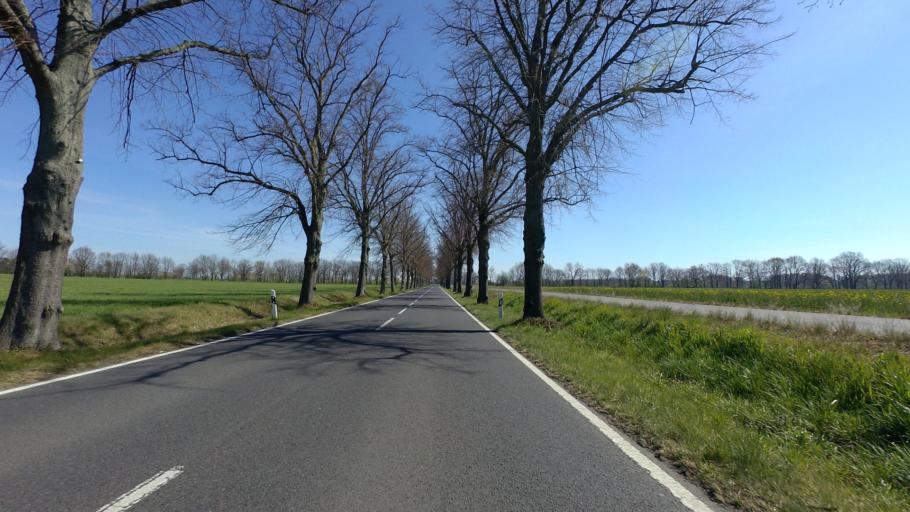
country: DE
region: Brandenburg
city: Schonefeld
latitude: 52.3472
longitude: 13.5327
